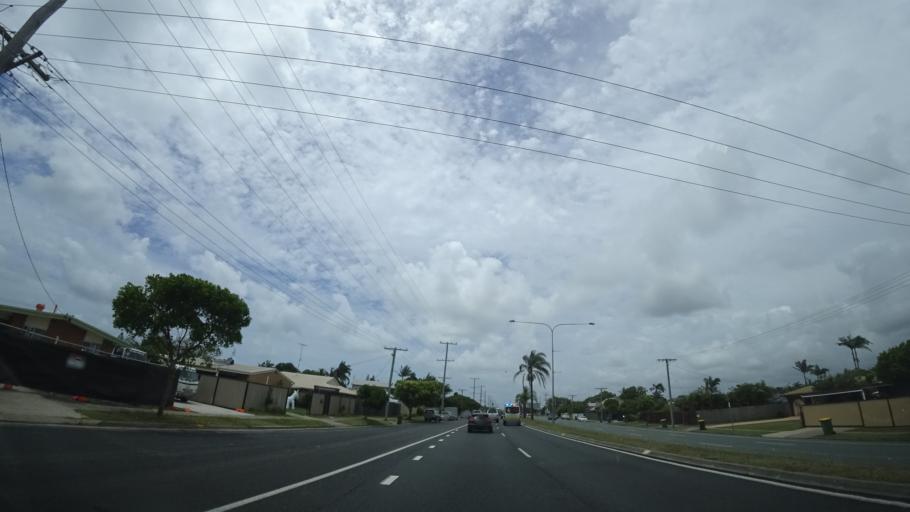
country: AU
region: Queensland
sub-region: Sunshine Coast
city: Mooloolaba
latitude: -26.7068
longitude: 153.1303
